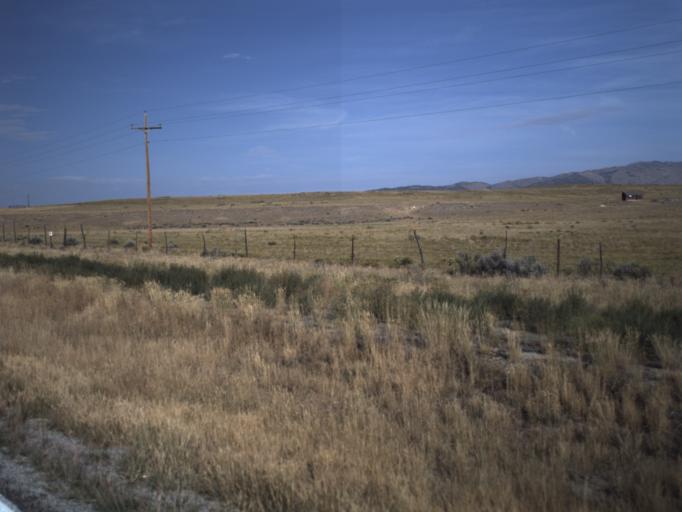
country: US
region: Idaho
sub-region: Oneida County
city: Malad City
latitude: 41.9654
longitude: -113.0490
